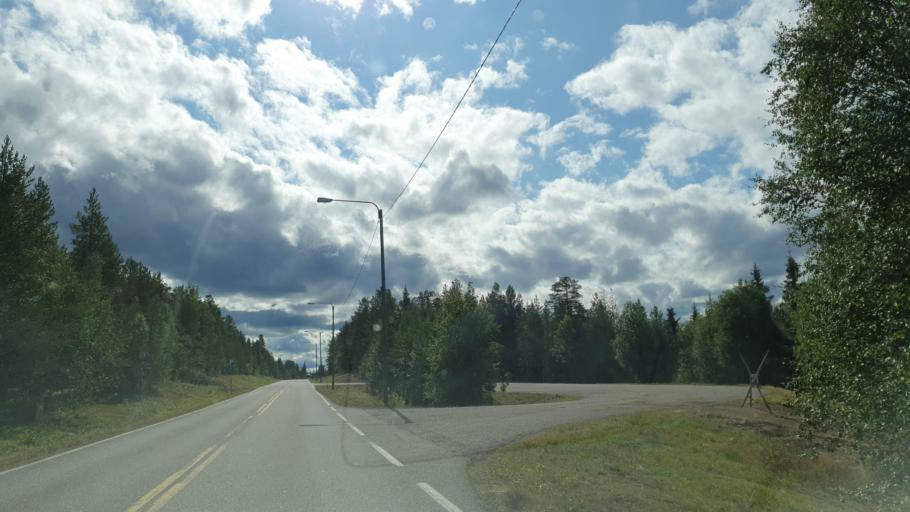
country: FI
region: Lapland
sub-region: Tunturi-Lappi
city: Muonio
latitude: 67.8886
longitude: 24.2151
